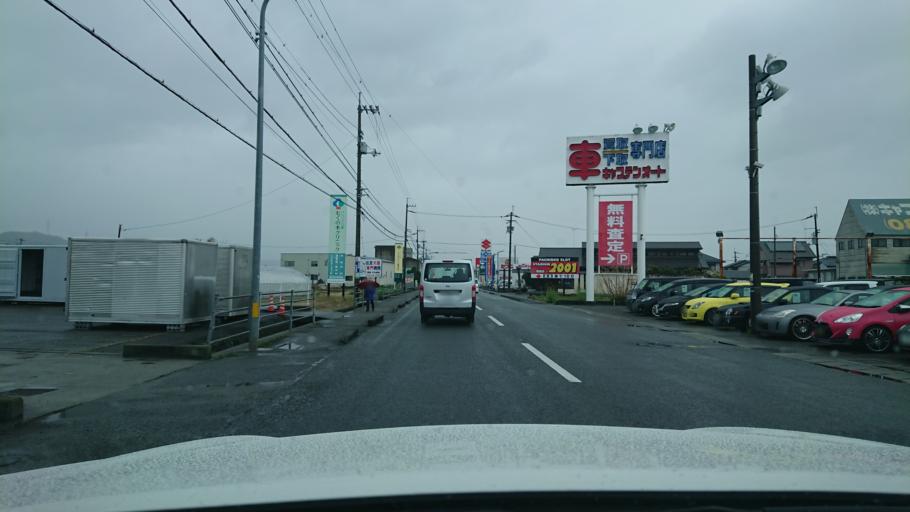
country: JP
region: Tokushima
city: Ishii
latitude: 34.0855
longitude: 134.4828
